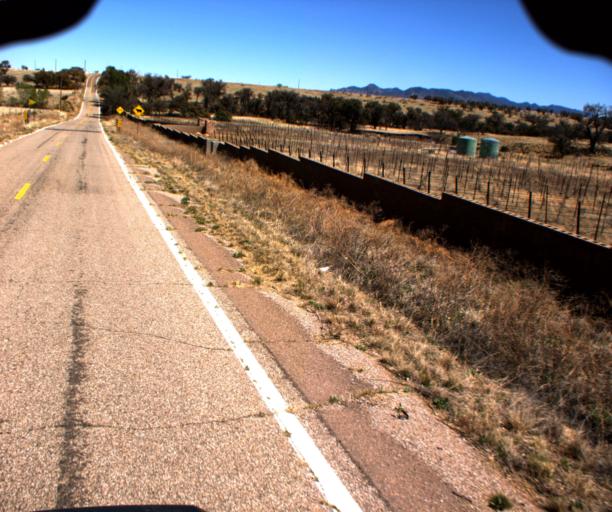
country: US
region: Arizona
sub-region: Cochise County
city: Huachuca City
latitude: 31.6007
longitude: -110.5641
